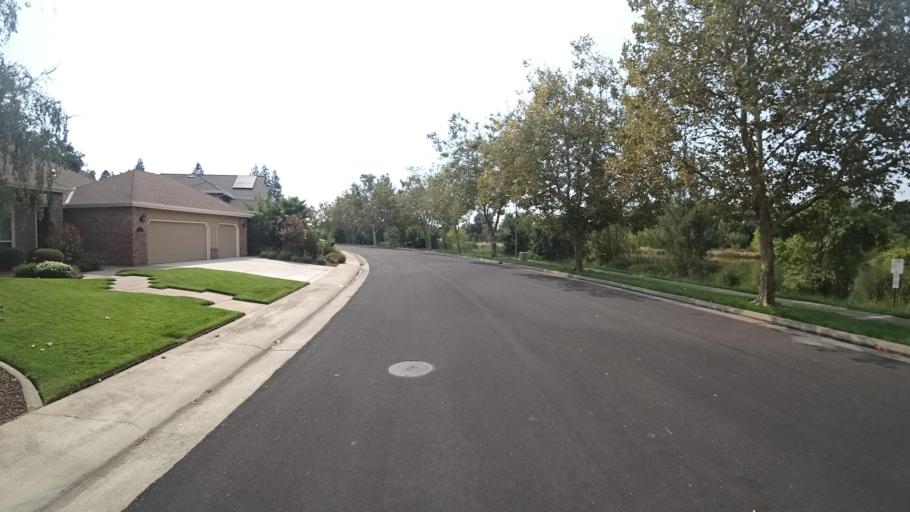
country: US
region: California
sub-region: Sacramento County
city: Elk Grove
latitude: 38.4254
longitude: -121.3774
